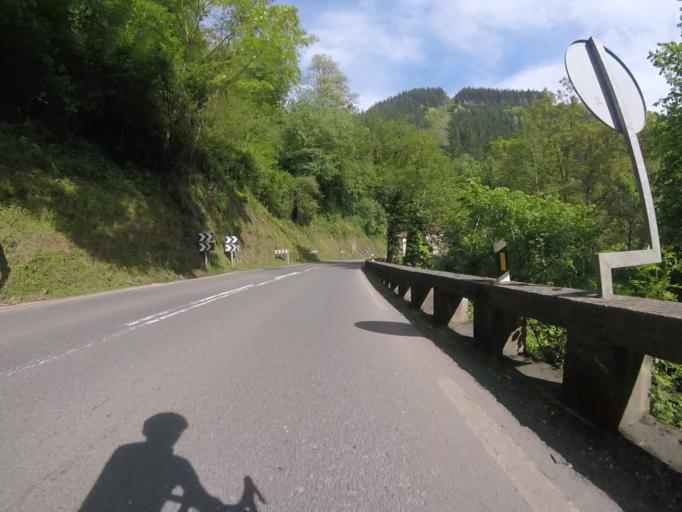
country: ES
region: Basque Country
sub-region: Provincia de Guipuzcoa
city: Azkoitia
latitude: 43.1545
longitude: -2.3419
